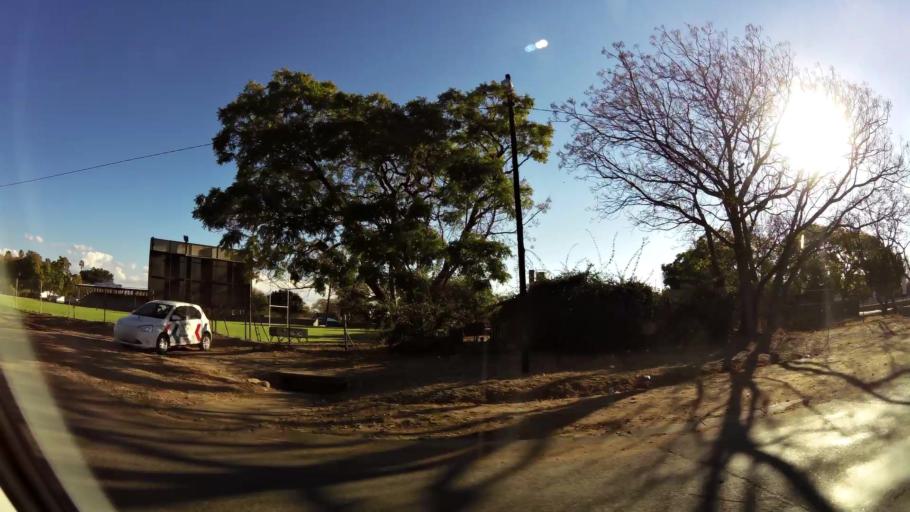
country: ZA
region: Limpopo
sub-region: Capricorn District Municipality
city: Polokwane
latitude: -23.8993
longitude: 29.4558
